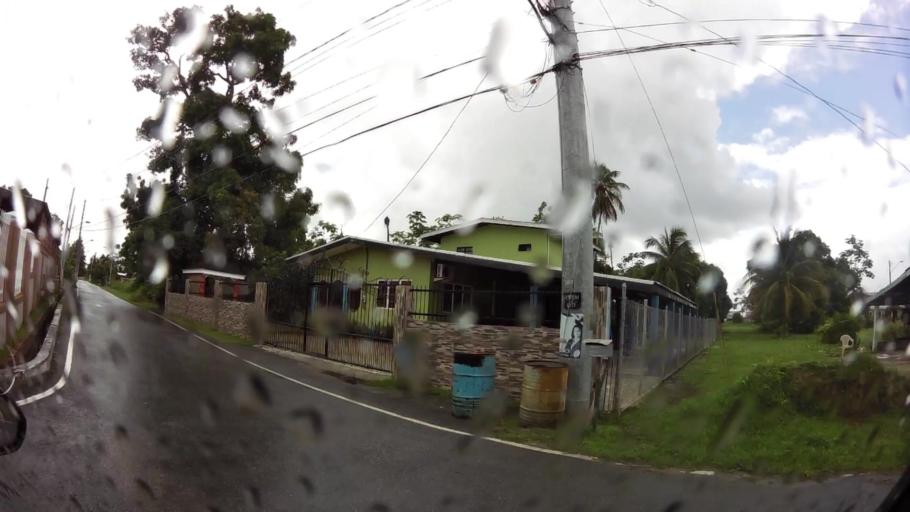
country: TT
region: Tunapuna/Piarco
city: Arouca
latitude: 10.6134
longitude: -61.3510
